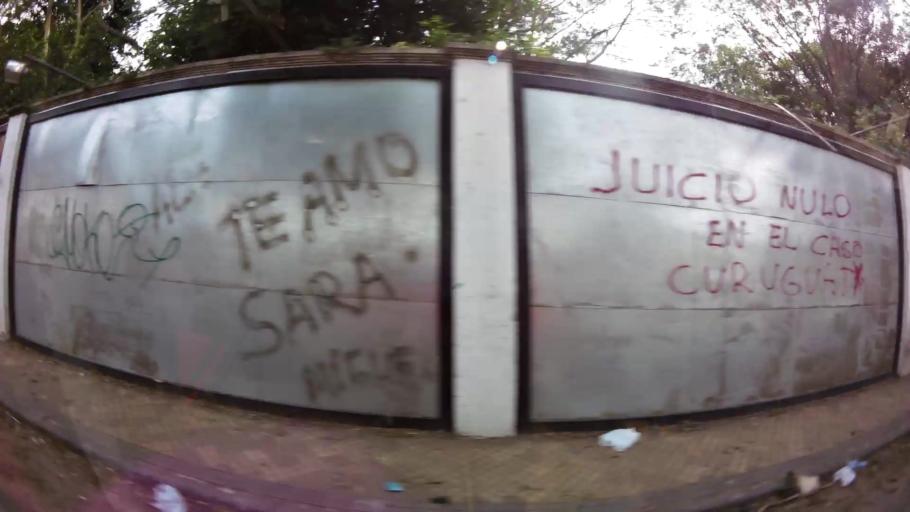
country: PY
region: Asuncion
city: Asuncion
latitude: -25.2702
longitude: -57.5626
